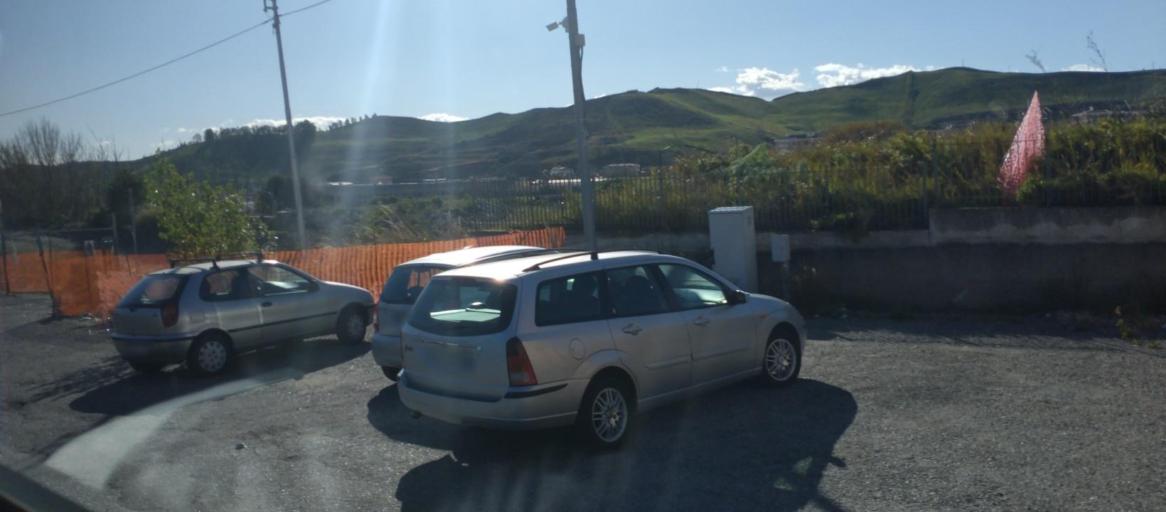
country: IT
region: Calabria
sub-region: Provincia di Catanzaro
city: Catanzaro
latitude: 38.8899
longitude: 16.6026
